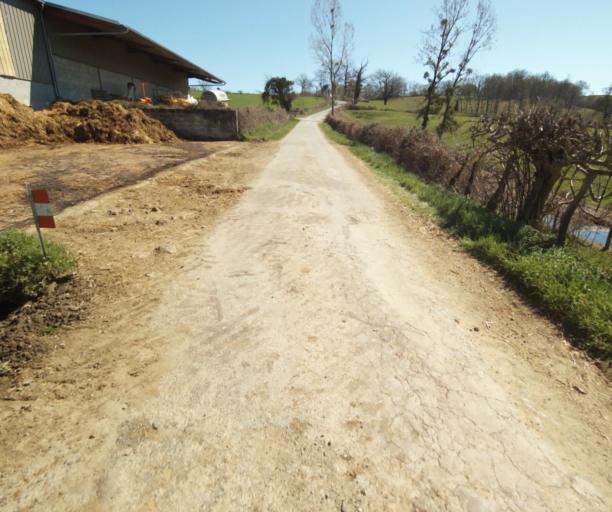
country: FR
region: Limousin
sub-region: Departement de la Correze
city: Chamboulive
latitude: 45.4464
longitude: 1.6768
